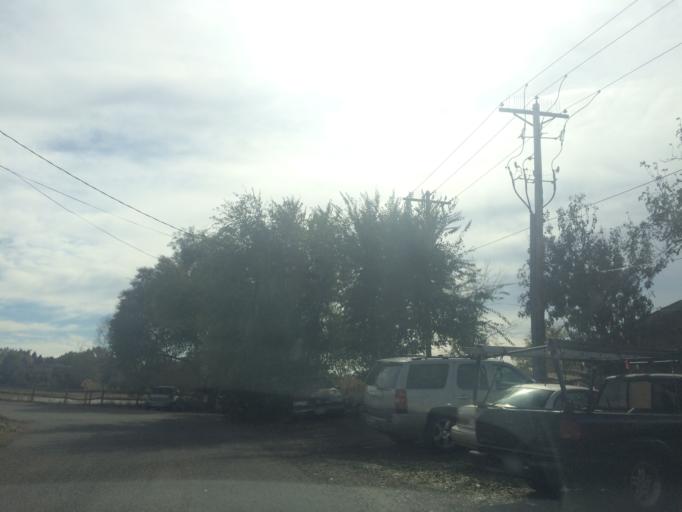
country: US
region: Colorado
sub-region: Boulder County
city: Gunbarrel
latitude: 40.0130
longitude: -105.2065
